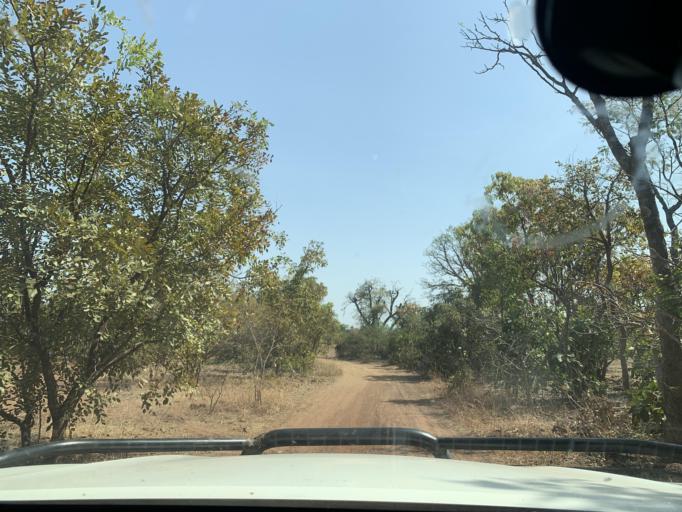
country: ML
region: Sikasso
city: Kolondieba
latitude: 10.8346
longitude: -6.7890
